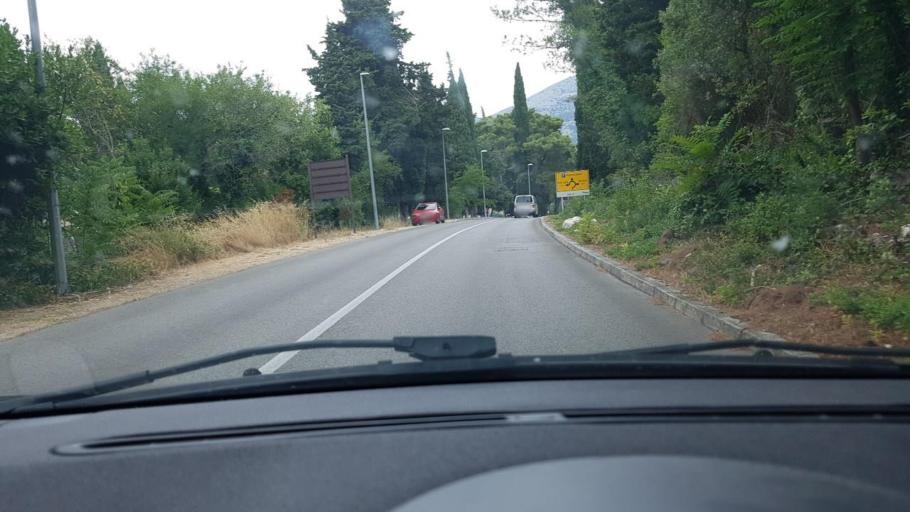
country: HR
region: Dubrovacko-Neretvanska
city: Korcula
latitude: 42.9540
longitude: 17.1313
